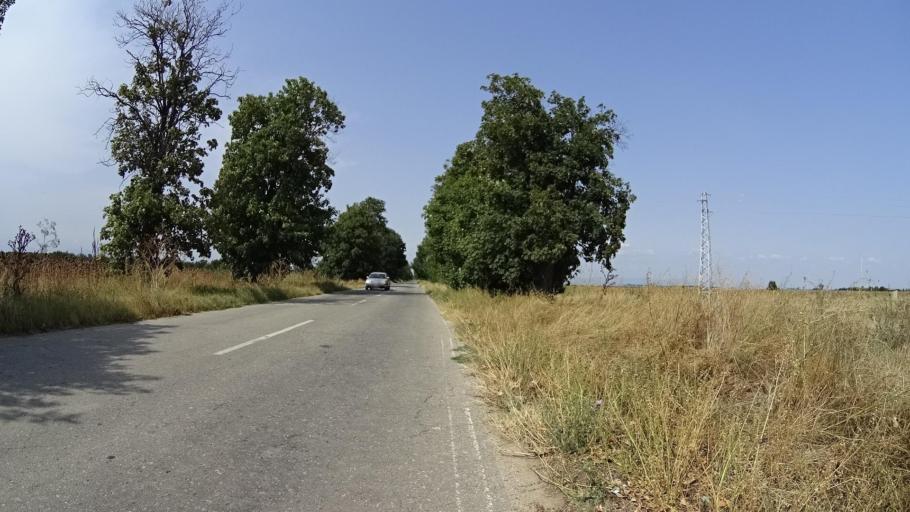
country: BG
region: Plovdiv
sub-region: Obshtina Kaloyanovo
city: Kaloyanovo
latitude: 42.2550
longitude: 24.7989
